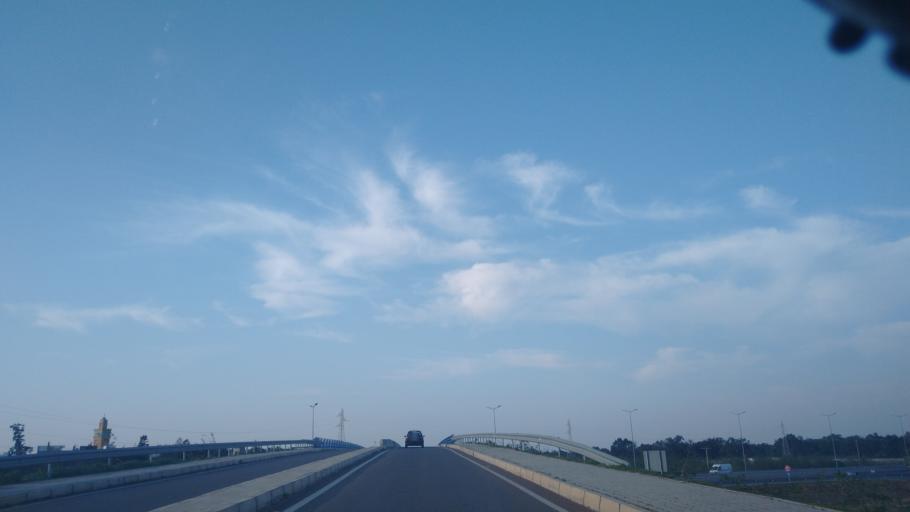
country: MA
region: Rabat-Sale-Zemmour-Zaer
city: Sale
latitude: 33.9994
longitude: -6.7189
